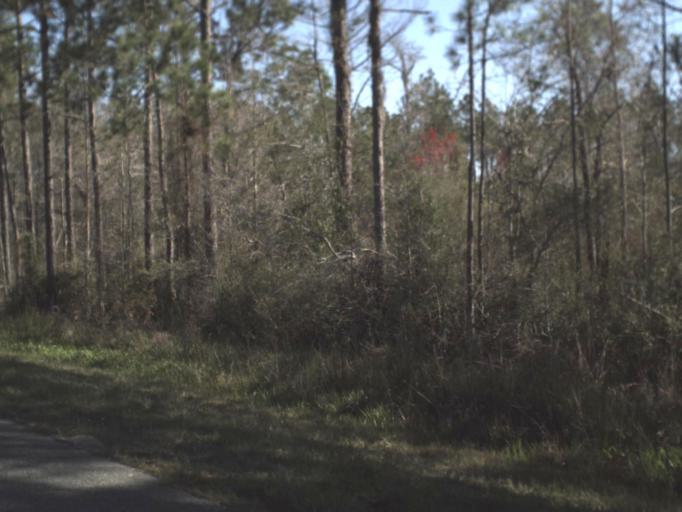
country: US
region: Florida
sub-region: Leon County
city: Woodville
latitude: 30.2323
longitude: -84.0426
